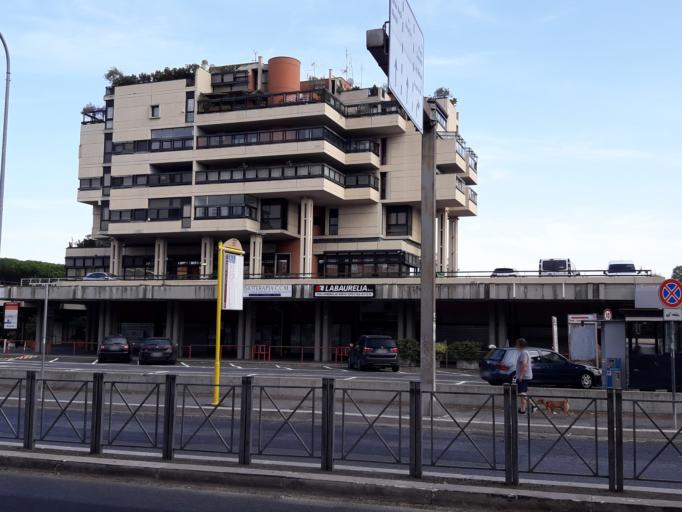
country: VA
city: Vatican City
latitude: 41.8987
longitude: 12.4256
